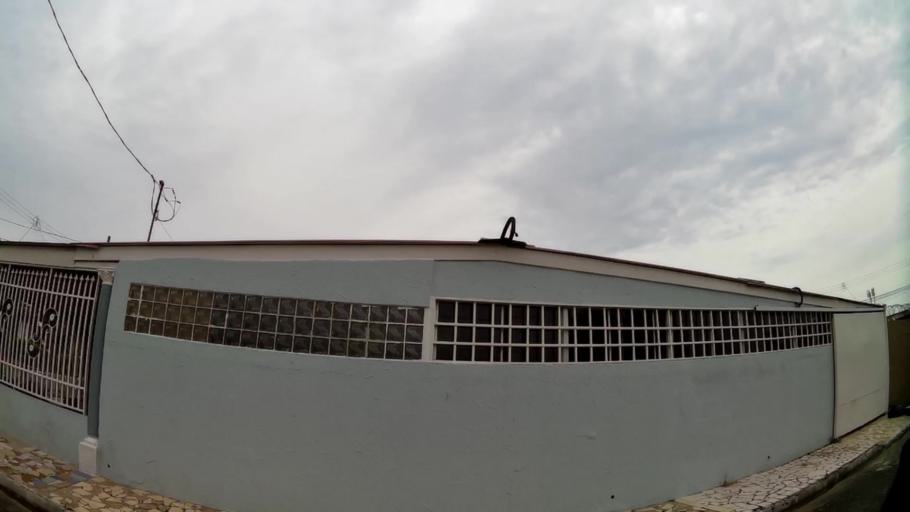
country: PA
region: Panama
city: San Miguelito
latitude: 9.0477
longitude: -79.4470
